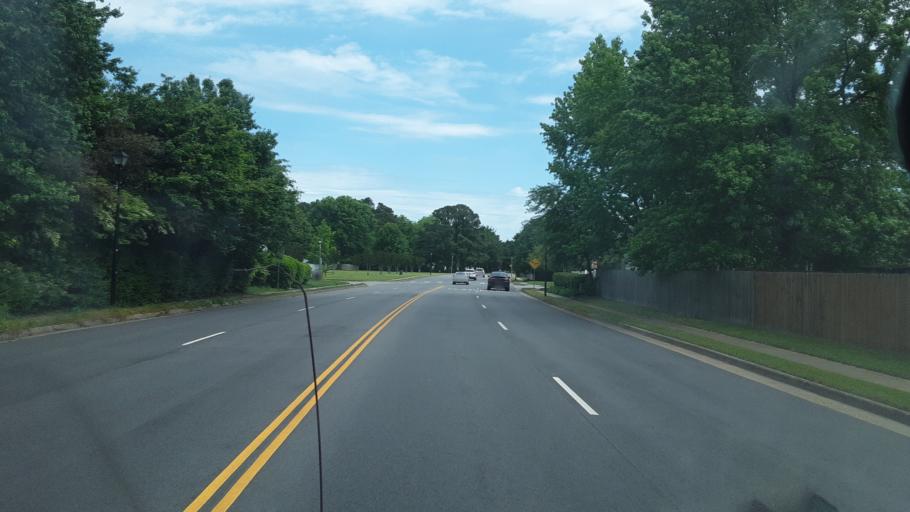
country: US
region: Virginia
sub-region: City of Virginia Beach
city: Virginia Beach
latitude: 36.7801
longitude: -75.9962
